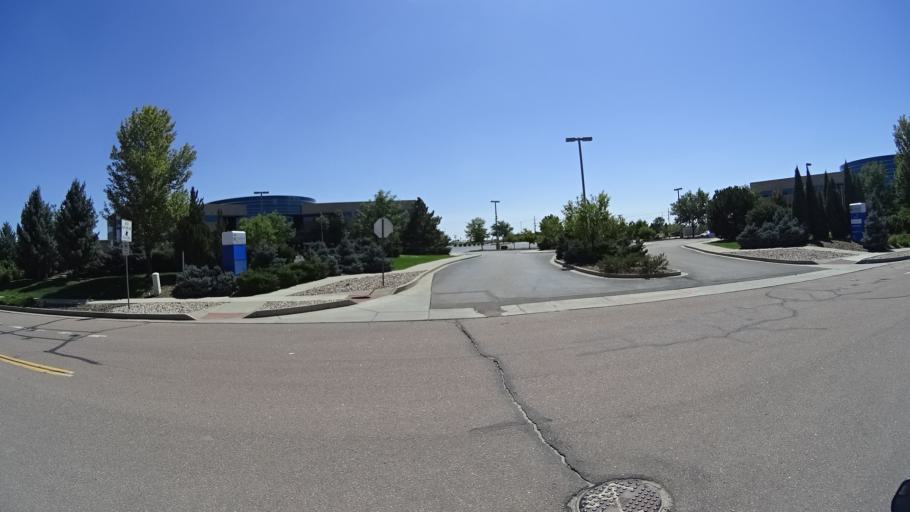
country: US
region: Colorado
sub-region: El Paso County
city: Cimarron Hills
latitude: 38.8410
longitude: -104.7254
